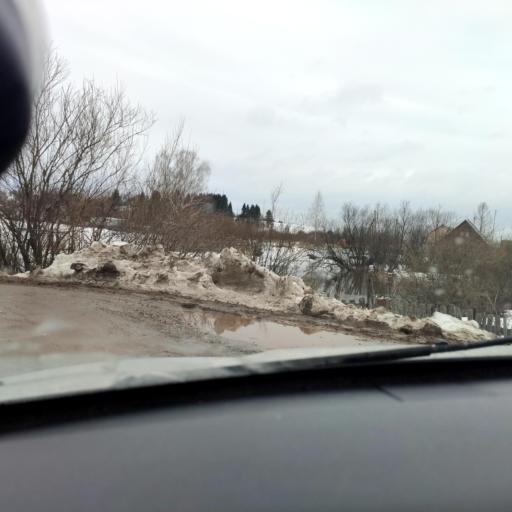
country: RU
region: Perm
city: Lobanovo
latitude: 57.8537
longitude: 56.3443
